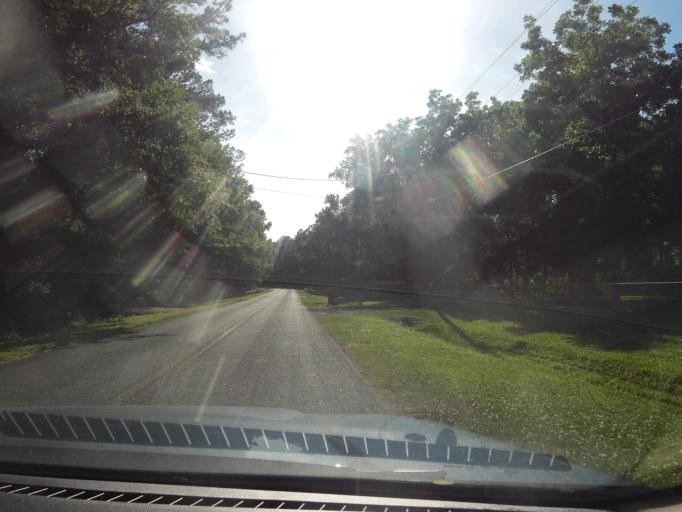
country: US
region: Florida
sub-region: Nassau County
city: Nassau Village-Ratliff
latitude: 30.4879
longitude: -81.8322
